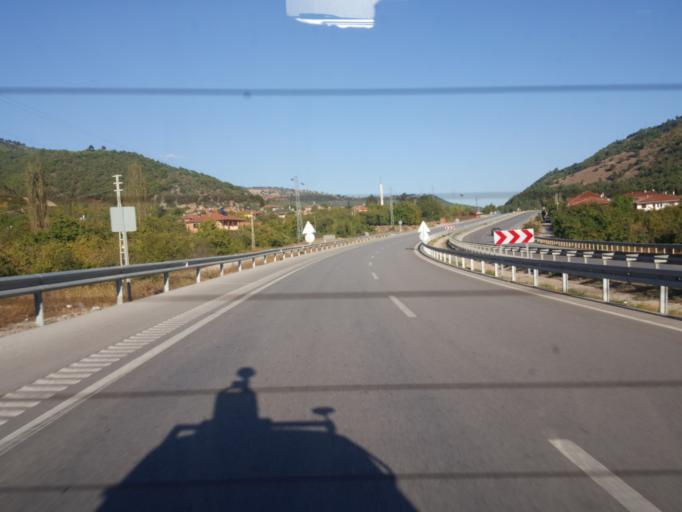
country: TR
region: Amasya
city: Akdag
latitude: 40.7500
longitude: 36.0462
